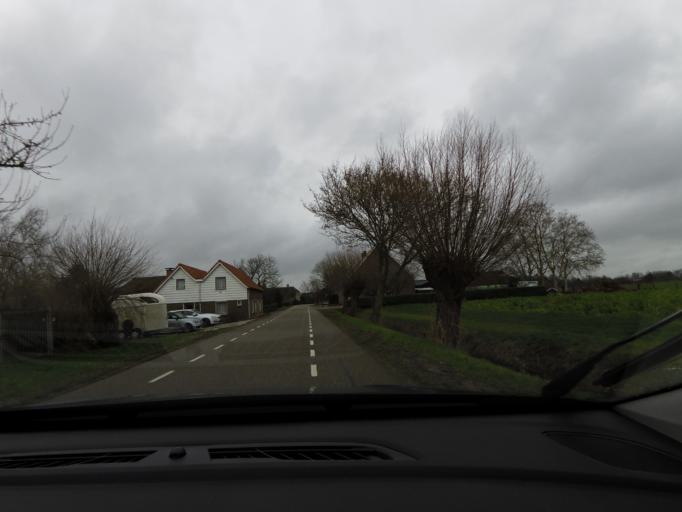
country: NL
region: North Brabant
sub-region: Gemeente Aalburg
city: Aalburg
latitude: 51.7607
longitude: 5.0904
